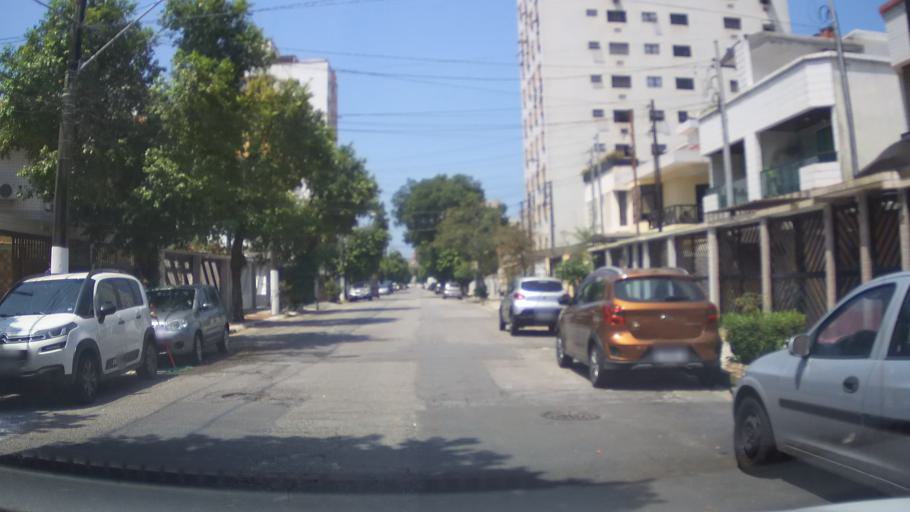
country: BR
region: Sao Paulo
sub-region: Santos
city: Santos
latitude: -23.9704
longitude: -46.3076
